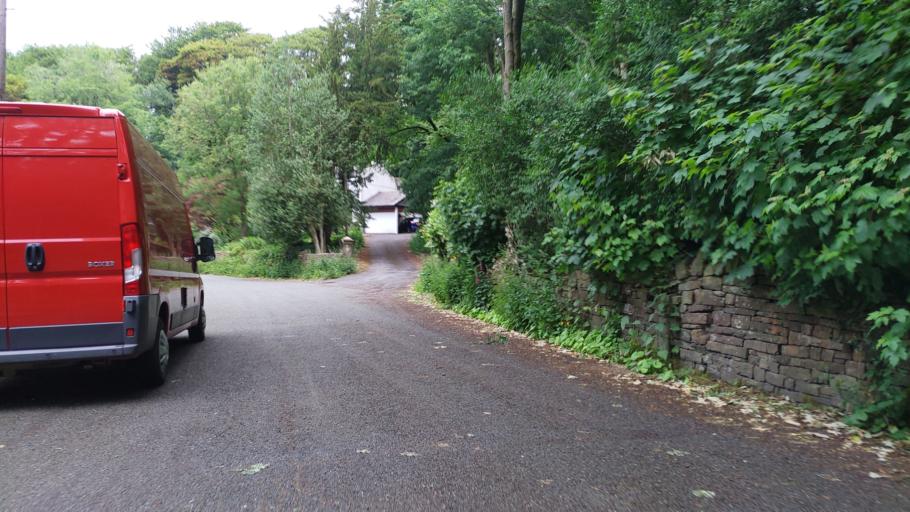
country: GB
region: England
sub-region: Lancashire
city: Chorley
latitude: 53.6882
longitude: -2.6053
